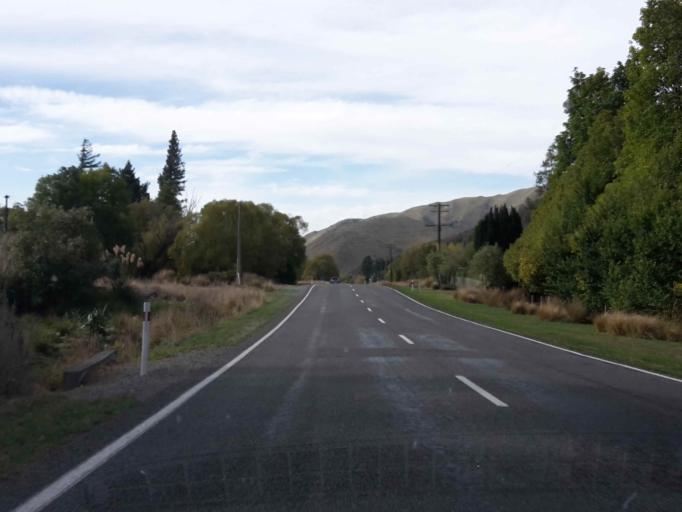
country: NZ
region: Canterbury
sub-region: Timaru District
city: Pleasant Point
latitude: -44.0845
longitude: 170.6583
